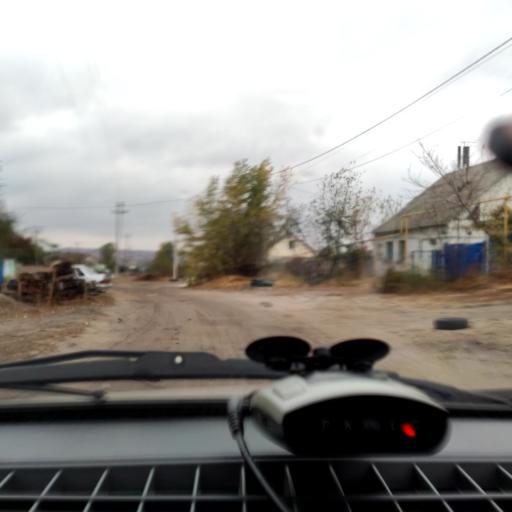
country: RU
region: Voronezj
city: Pridonskoy
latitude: 51.7022
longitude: 39.0711
